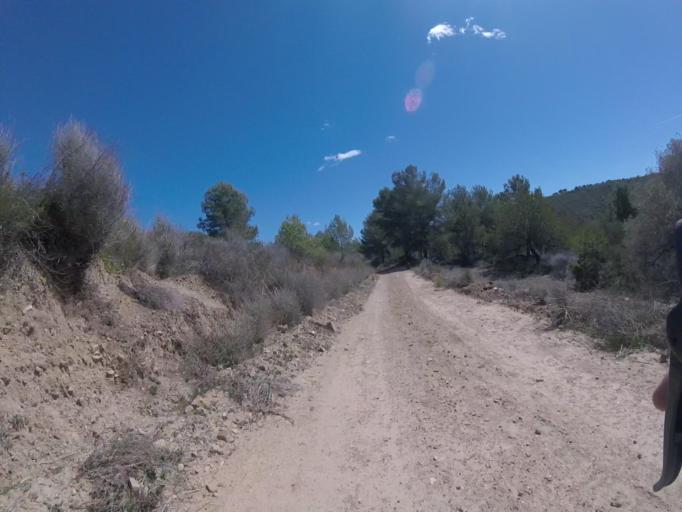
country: ES
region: Valencia
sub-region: Provincia de Castello
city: Cabanes
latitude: 40.1568
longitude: 0.1021
